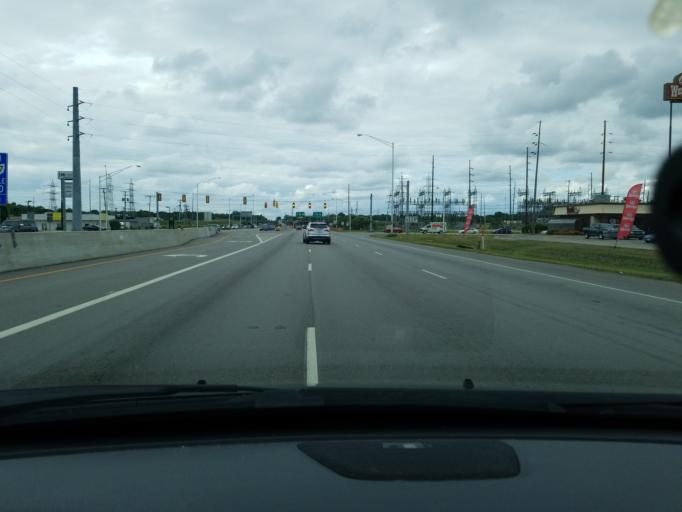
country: US
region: Ohio
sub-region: Lorain County
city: Sheffield
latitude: 41.3990
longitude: -82.1165
